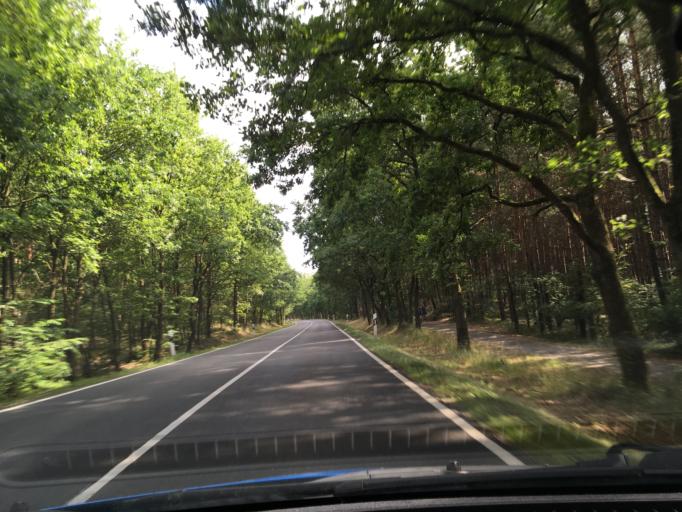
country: DE
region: Mecklenburg-Vorpommern
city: Lubtheen
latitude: 53.2903
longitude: 11.0924
